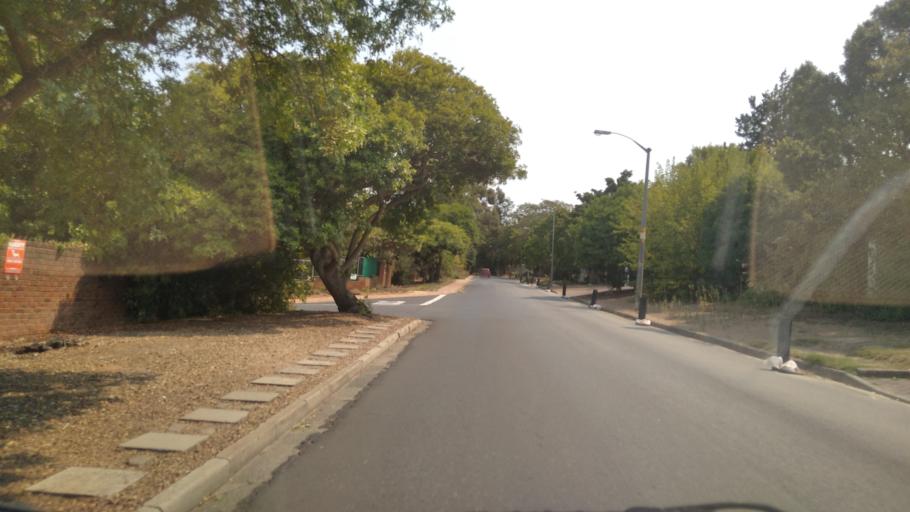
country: ZA
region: Western Cape
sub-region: City of Cape Town
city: Kraaifontein
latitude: -33.8182
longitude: 18.6593
